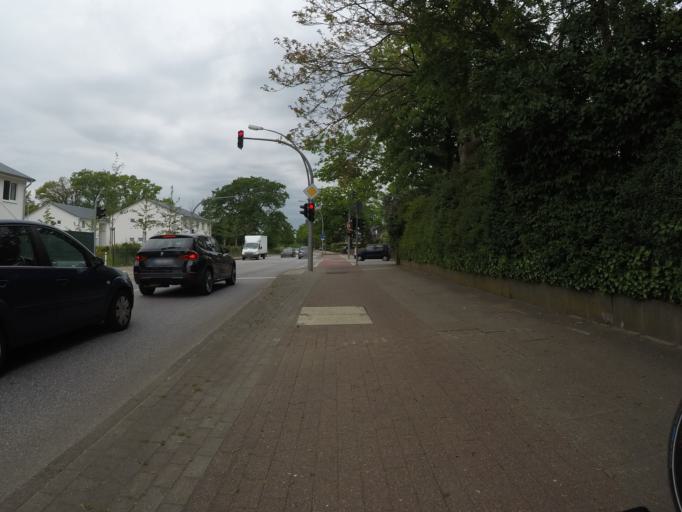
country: DE
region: Schleswig-Holstein
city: Norderstedt
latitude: 53.6899
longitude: 9.9779
